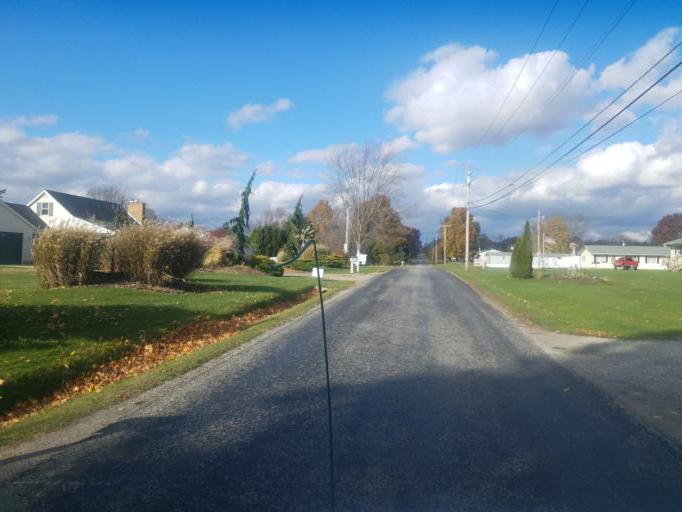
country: US
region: Ohio
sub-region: Wayne County
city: Orrville
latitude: 40.8251
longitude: -81.7746
